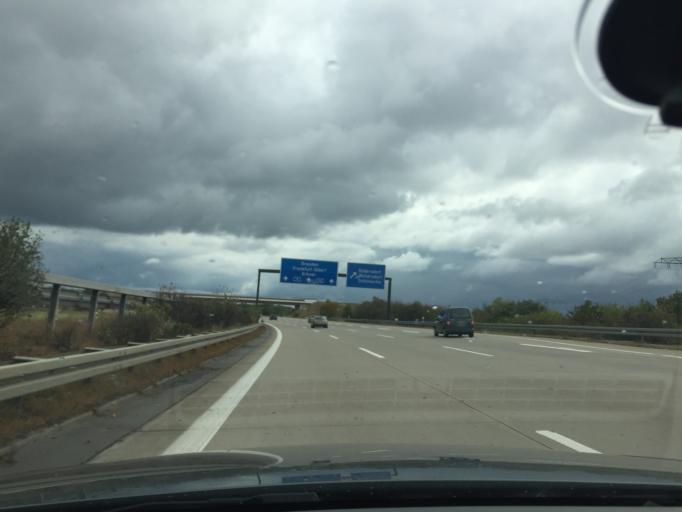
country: DE
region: Brandenburg
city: Woltersdorf
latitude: 52.4790
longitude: 13.7565
